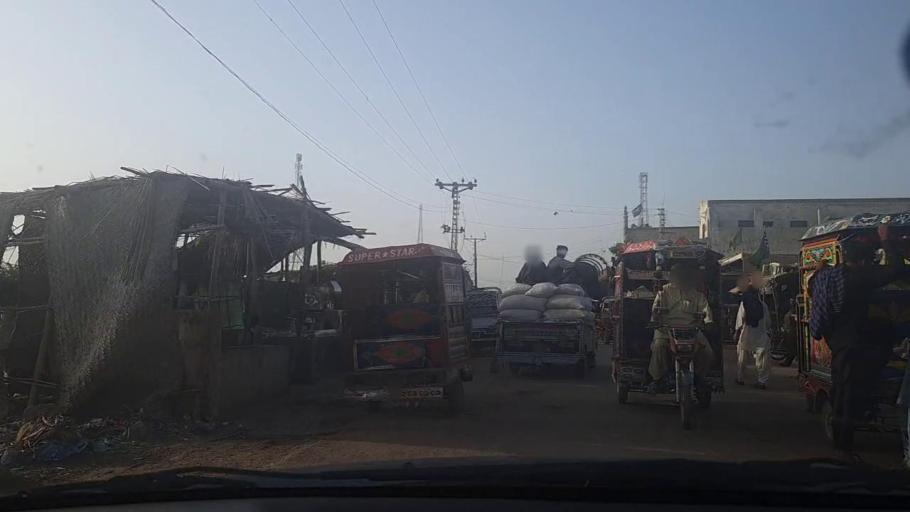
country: PK
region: Sindh
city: Keti Bandar
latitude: 24.2992
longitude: 67.6072
